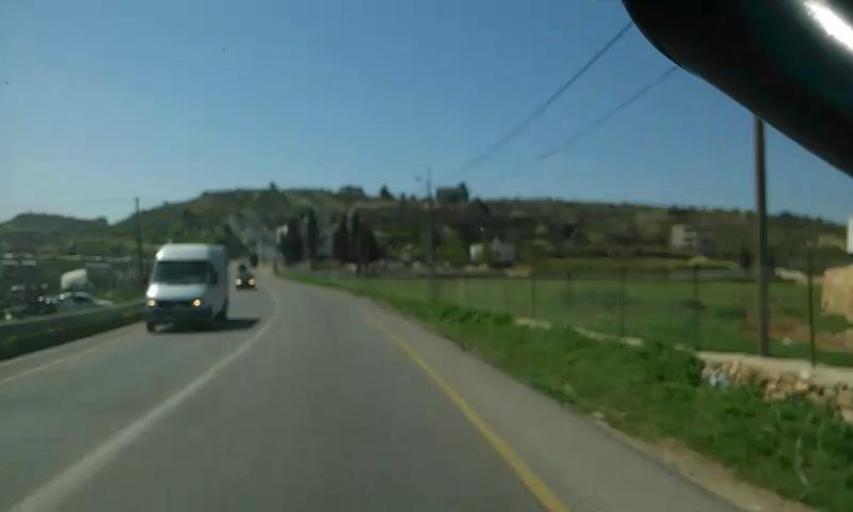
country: PS
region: West Bank
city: Bayt Ummar
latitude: 31.6132
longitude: 35.1137
